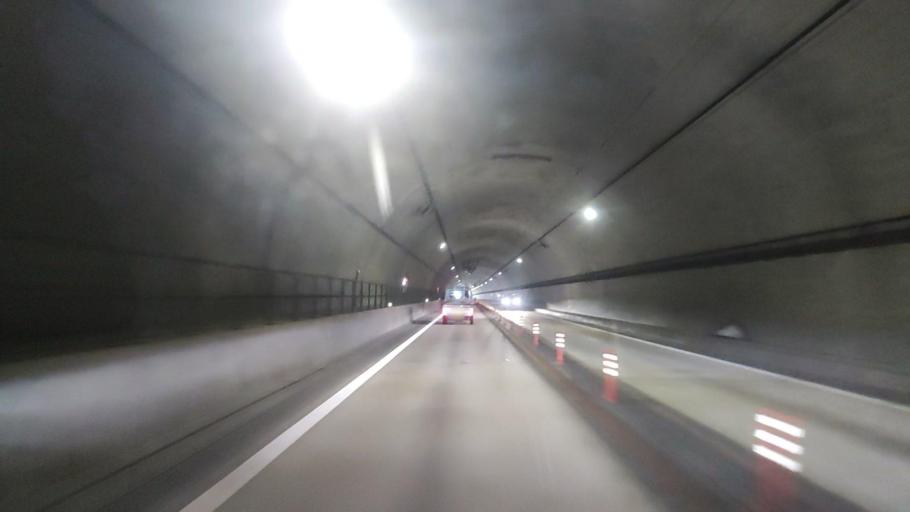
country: JP
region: Wakayama
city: Tanabe
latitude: 33.6288
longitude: 135.4152
